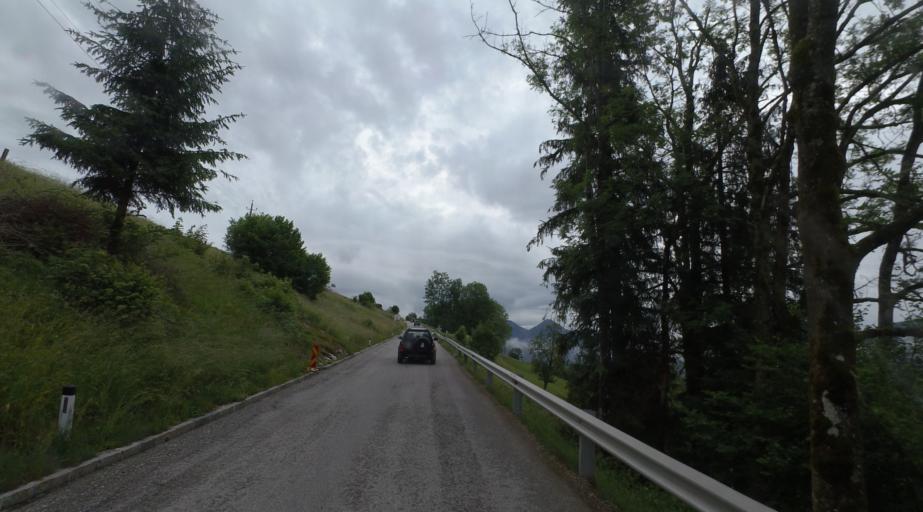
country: AT
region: Upper Austria
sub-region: Politischer Bezirk Kirchdorf an der Krems
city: Micheldorf in Oberoesterreich
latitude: 47.9217
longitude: 14.1573
